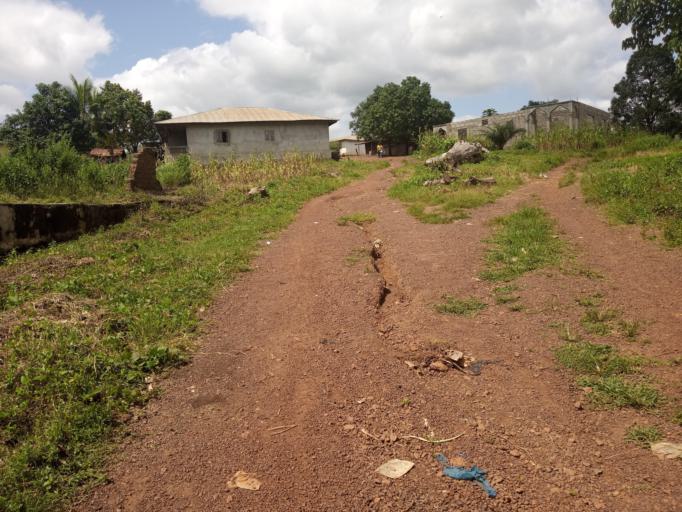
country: SL
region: Northern Province
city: Kamakwie
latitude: 9.4920
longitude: -12.2446
